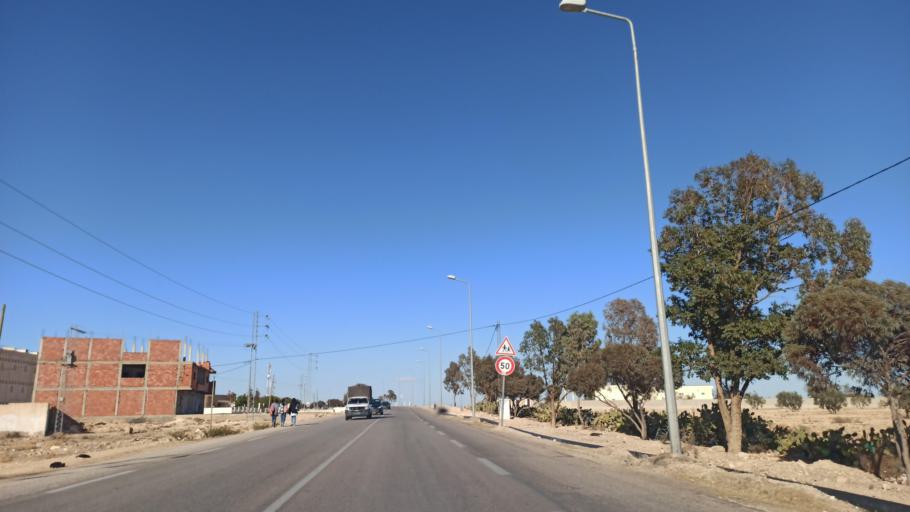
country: TN
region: Sidi Bu Zayd
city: Jilma
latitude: 35.2868
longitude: 9.4188
